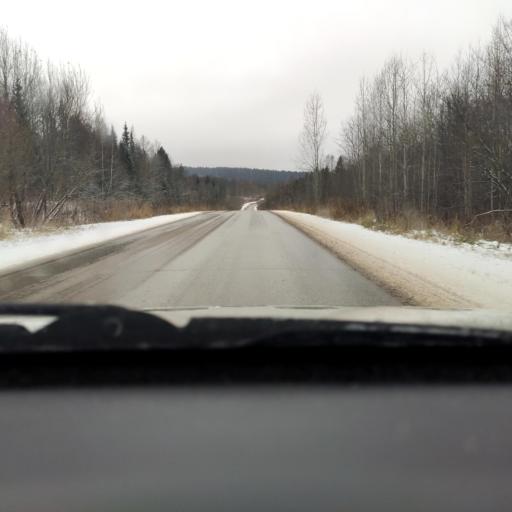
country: RU
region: Perm
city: Ferma
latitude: 57.9814
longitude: 56.3602
